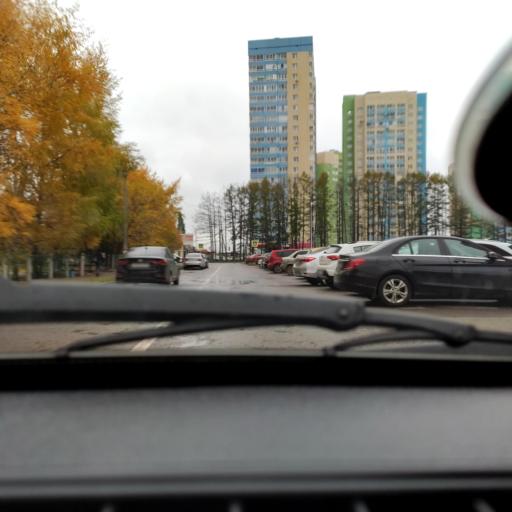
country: RU
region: Bashkortostan
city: Mikhaylovka
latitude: 54.7937
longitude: 55.8678
